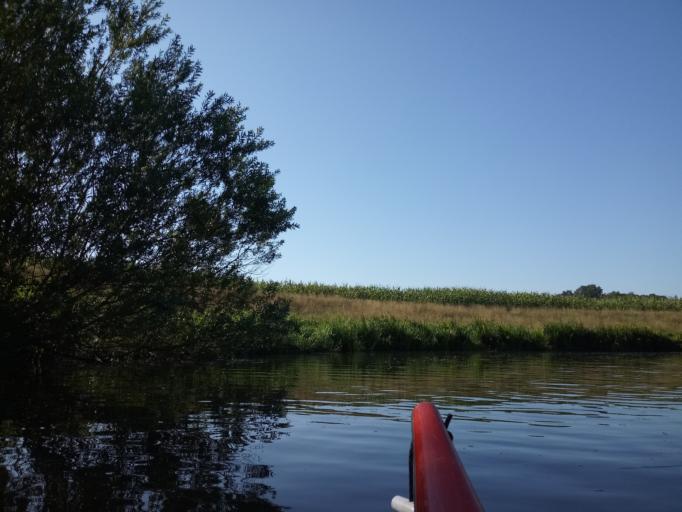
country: NL
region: Overijssel
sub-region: Gemeente Haaksbergen
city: Haaksbergen
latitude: 52.0890
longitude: 6.7338
